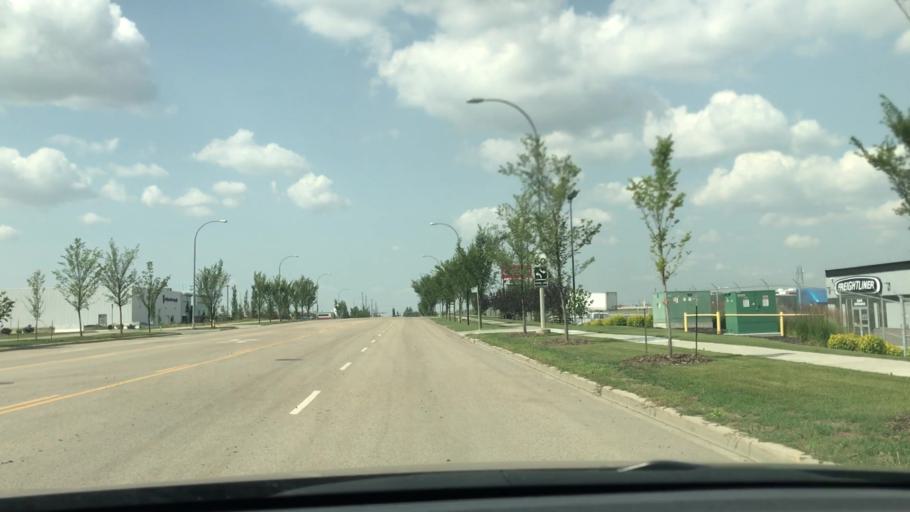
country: CA
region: Alberta
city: Edmonton
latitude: 53.4956
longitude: -113.4101
